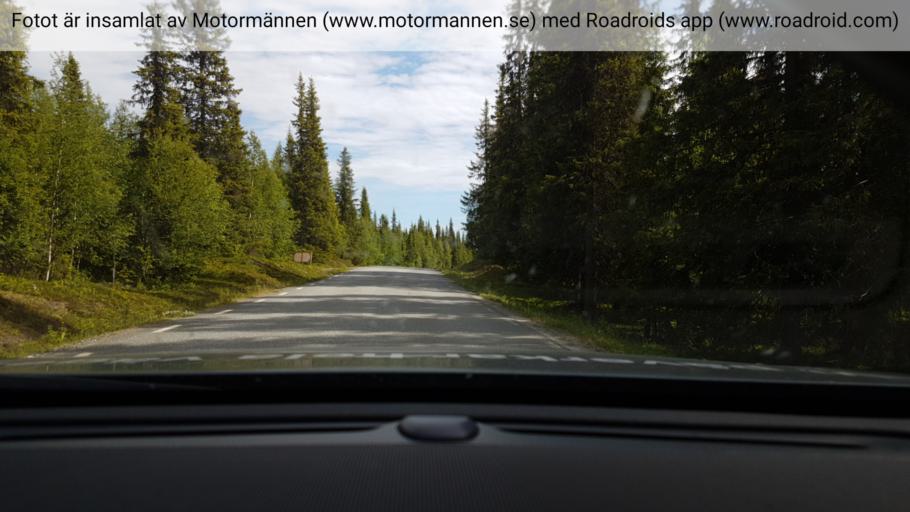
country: SE
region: Vaesterbotten
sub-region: Vilhelmina Kommun
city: Sjoberg
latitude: 65.2302
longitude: 16.0021
